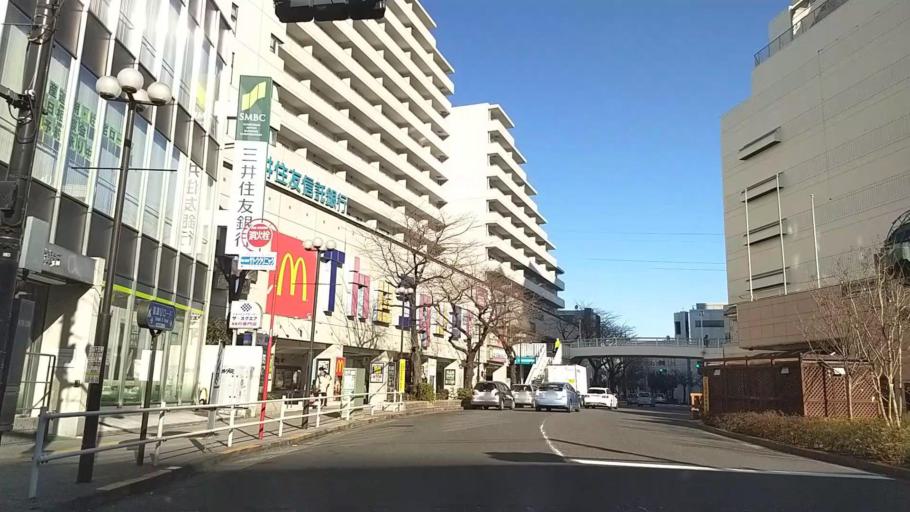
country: JP
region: Tokyo
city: Hino
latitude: 35.6508
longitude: 139.4464
